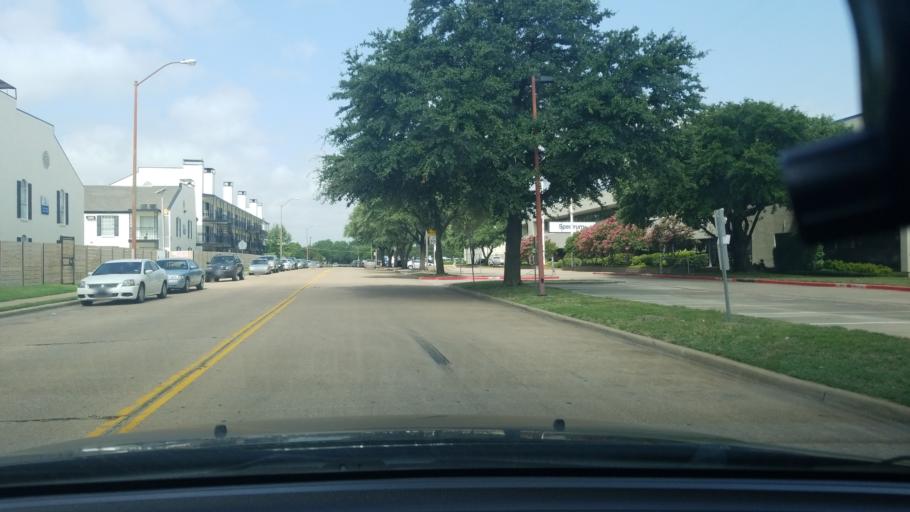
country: US
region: Texas
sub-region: Dallas County
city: Mesquite
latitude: 32.8028
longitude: -96.6885
